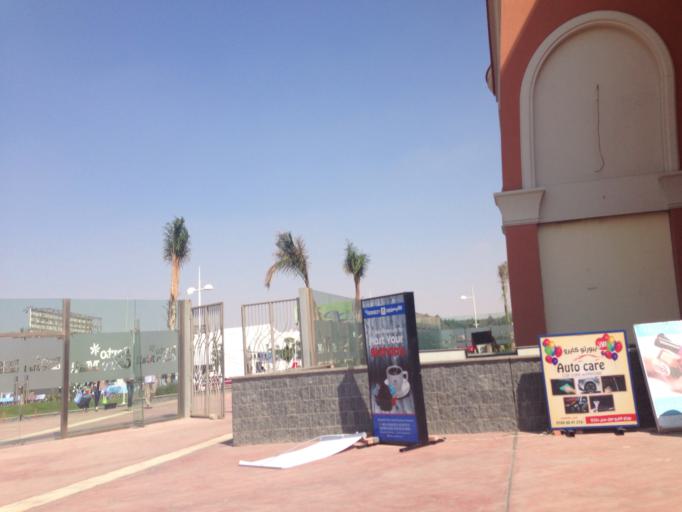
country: EG
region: Muhafazat al Qalyubiyah
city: Al Khankah
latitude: 30.0655
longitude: 31.4248
